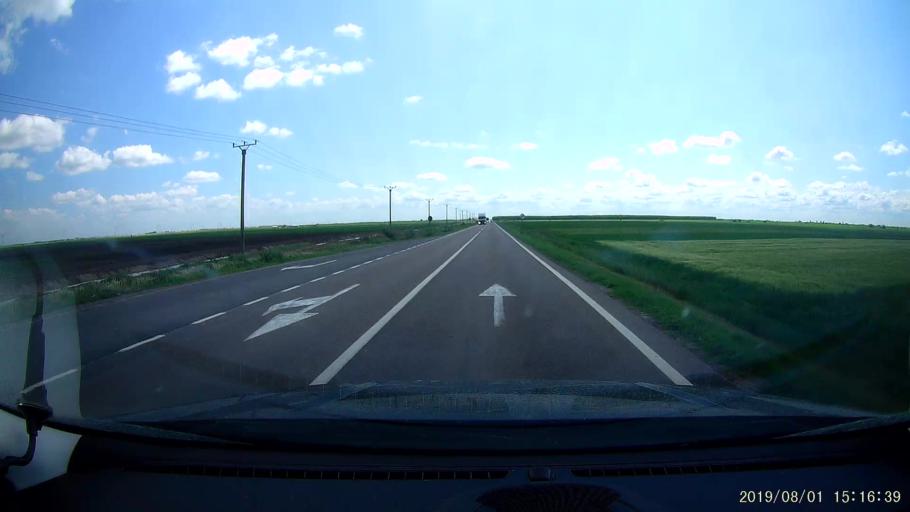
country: RO
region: Braila
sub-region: Comuna Unirea
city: Unirea
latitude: 45.1431
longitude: 27.8493
